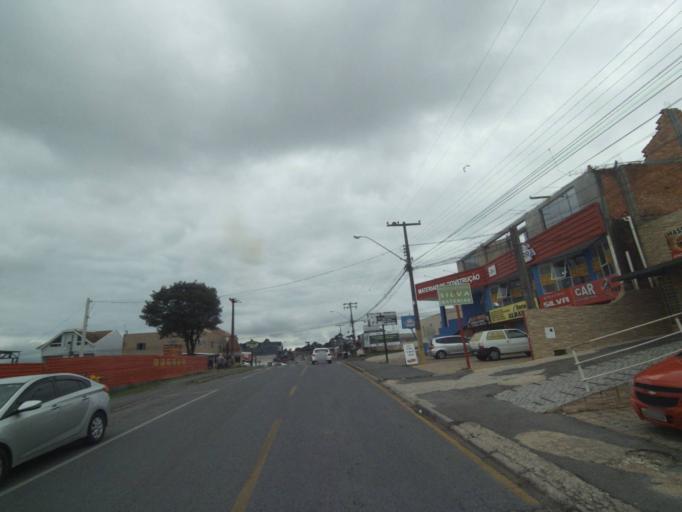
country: BR
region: Parana
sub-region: Quatro Barras
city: Quatro Barras
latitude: -25.3553
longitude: -49.1104
